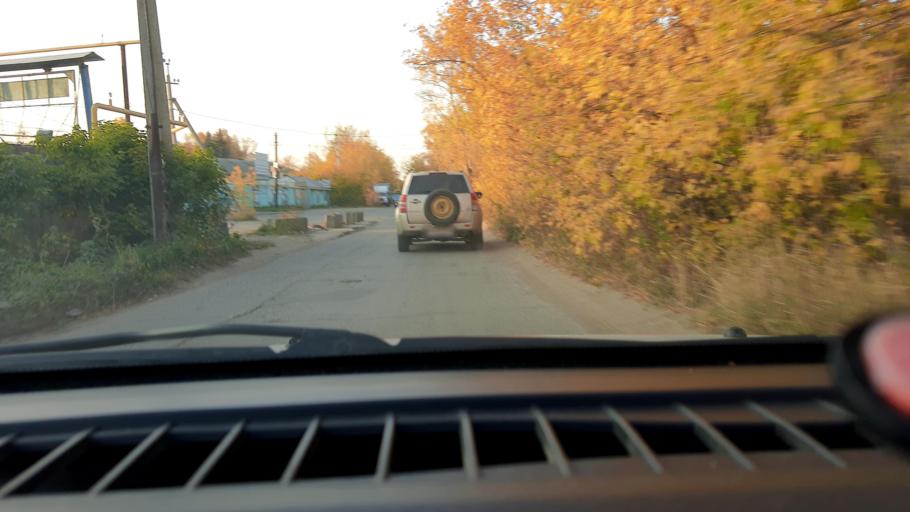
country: RU
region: Nizjnij Novgorod
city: Gorbatovka
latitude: 56.3098
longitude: 43.8280
